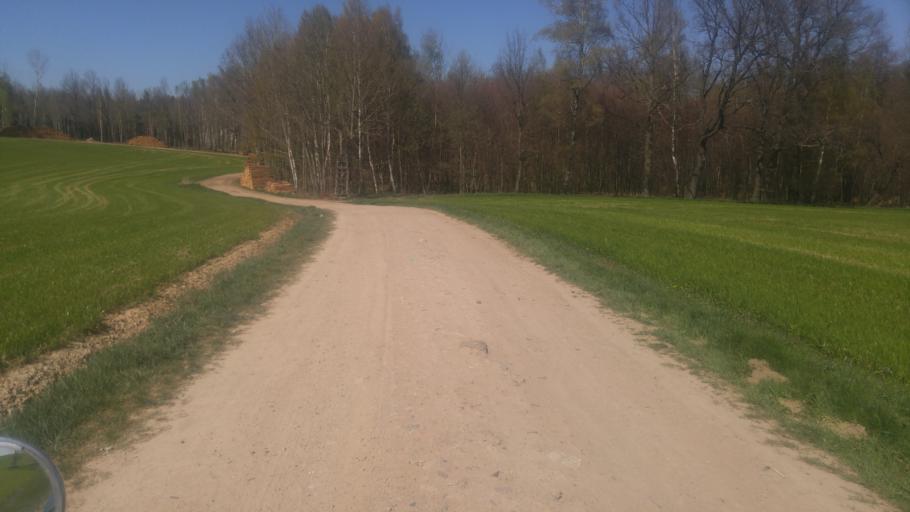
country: DE
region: Saxony
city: Altmittweida
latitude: 50.9487
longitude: 12.9620
